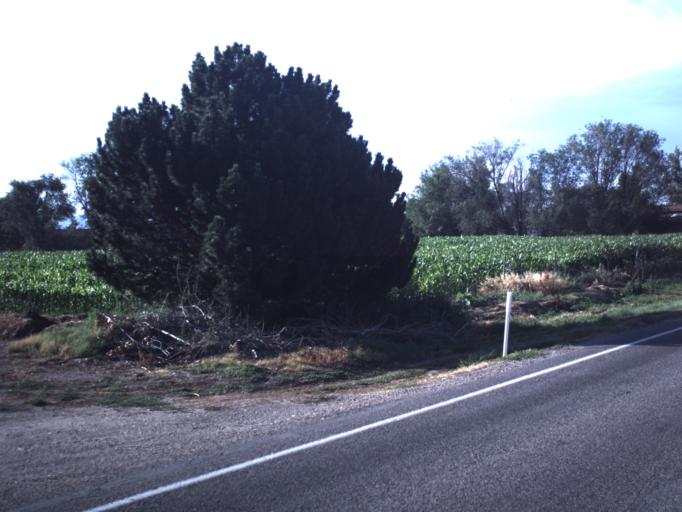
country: US
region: Utah
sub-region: Weber County
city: Plain City
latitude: 41.2644
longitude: -112.0924
